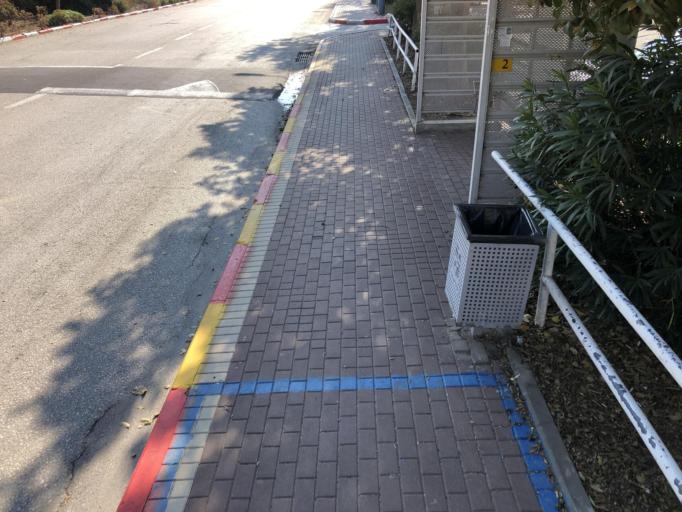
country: IL
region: Northern District
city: `Akko
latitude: 32.9226
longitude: 35.0968
